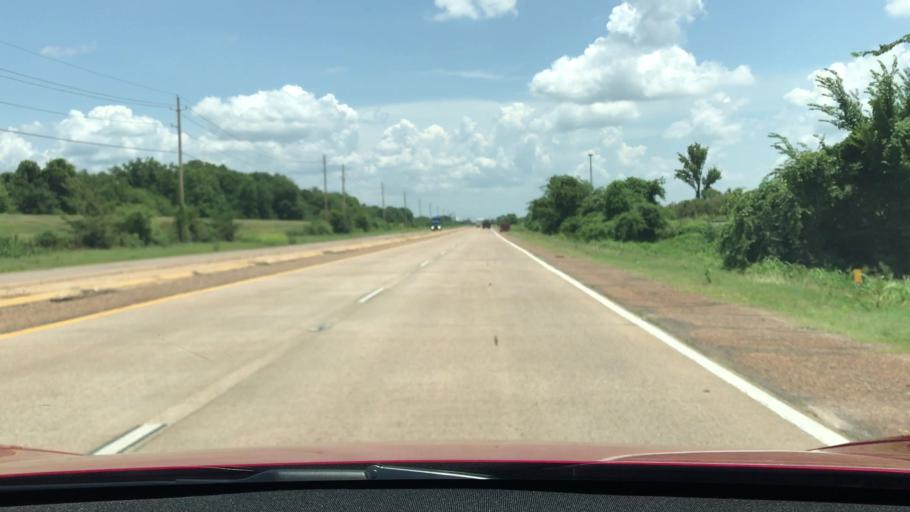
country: US
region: Louisiana
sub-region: Bossier Parish
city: Bossier City
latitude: 32.3867
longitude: -93.6768
